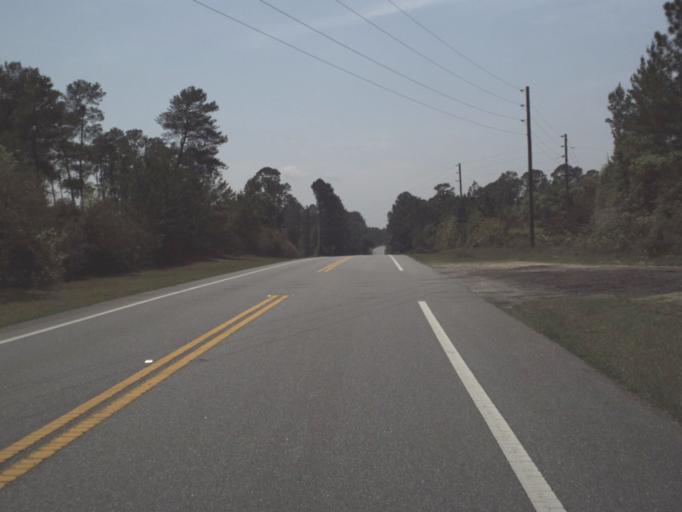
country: US
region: Florida
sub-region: Lake County
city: Astor
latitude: 29.1193
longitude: -81.6181
